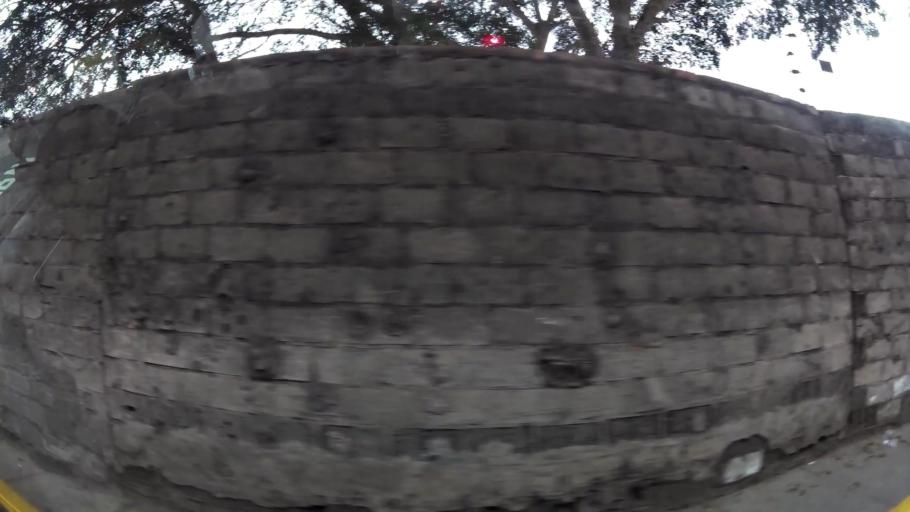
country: PE
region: Lima
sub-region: Lima
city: Surco
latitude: -12.1476
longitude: -76.9984
